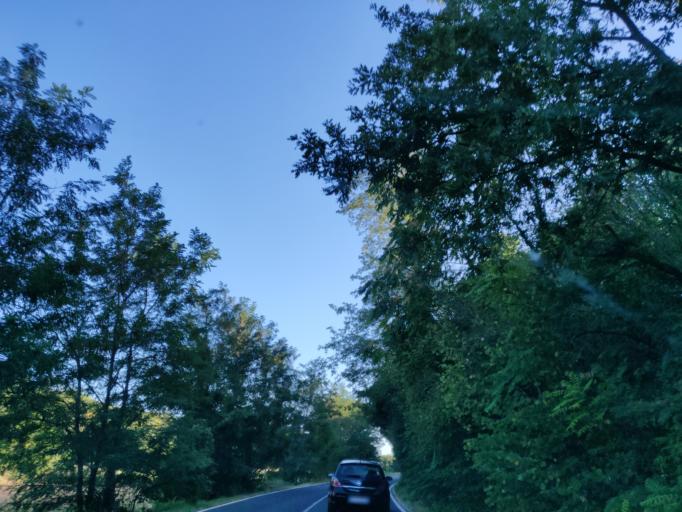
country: IT
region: Latium
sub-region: Provincia di Viterbo
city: Gradoli
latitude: 42.6514
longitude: 11.8431
